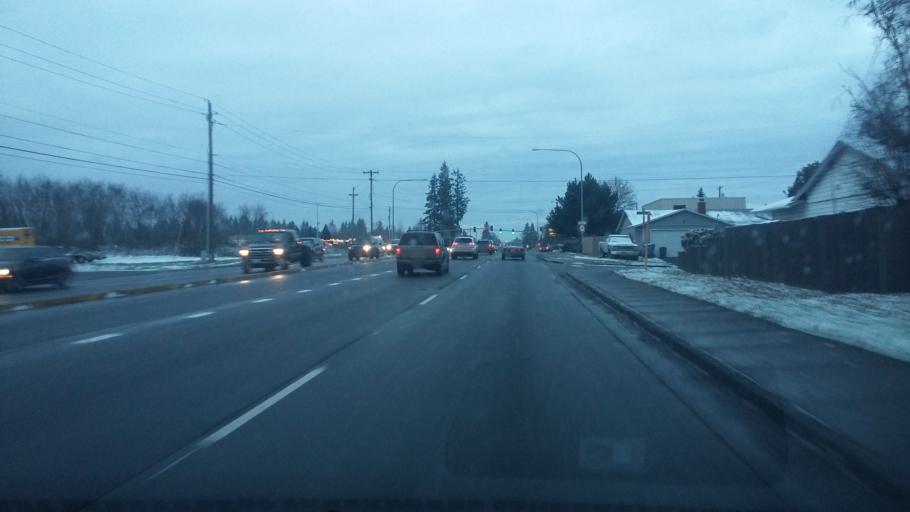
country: US
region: Washington
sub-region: Clark County
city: Orchards
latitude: 45.6800
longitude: -122.5525
